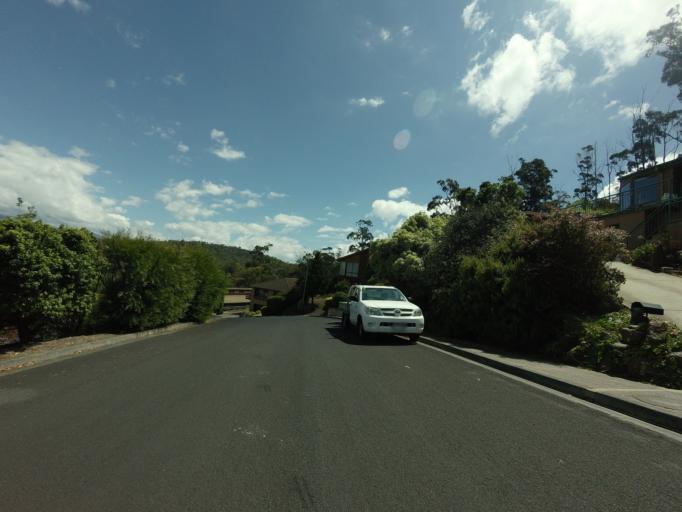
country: AU
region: Tasmania
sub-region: Clarence
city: Howrah
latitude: -42.8734
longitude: 147.4051
